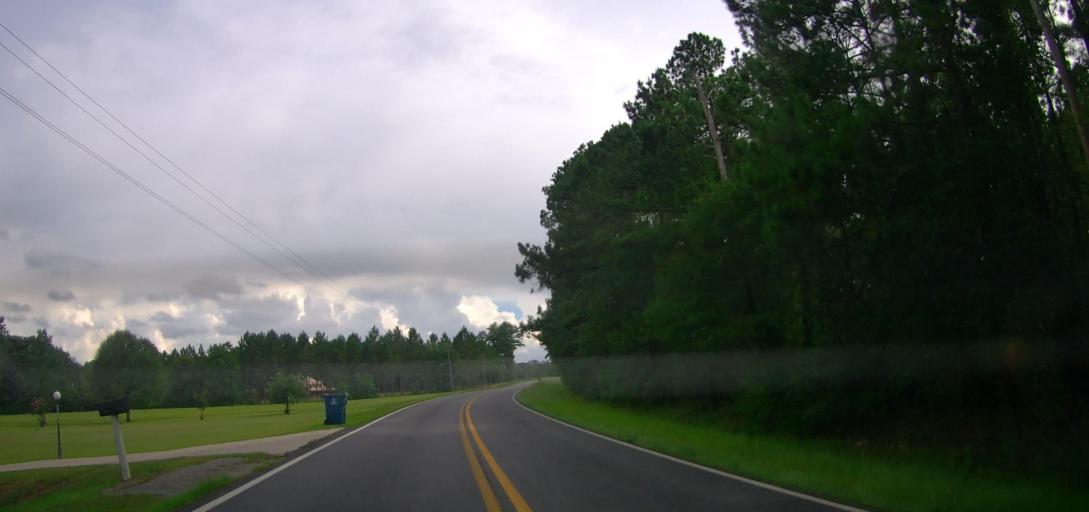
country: US
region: Georgia
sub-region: Wayne County
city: Jesup
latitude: 31.6743
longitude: -81.9181
